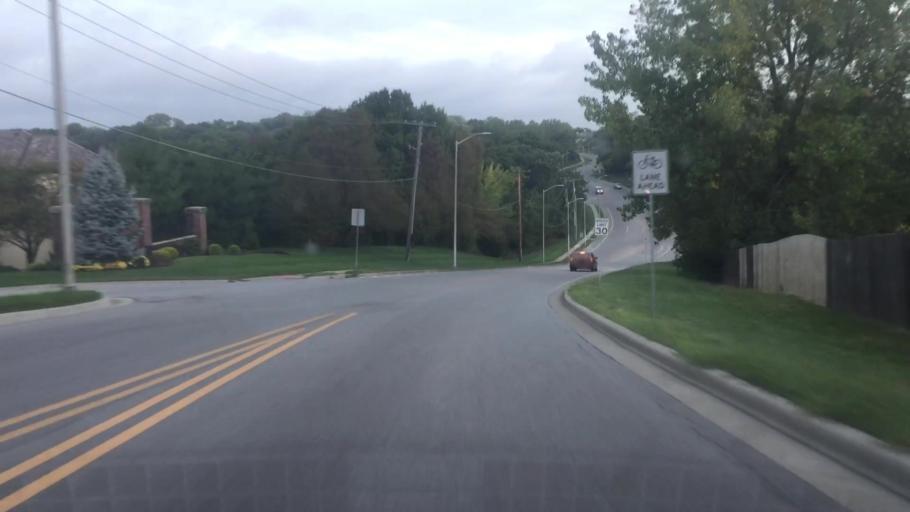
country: US
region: Kansas
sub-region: Johnson County
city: Shawnee
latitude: 39.0370
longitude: -94.7510
